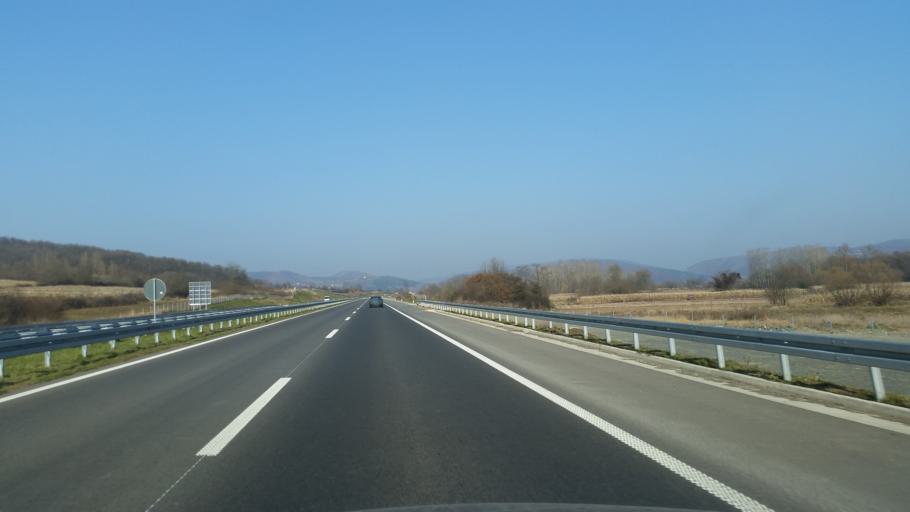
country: RS
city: Prislonica
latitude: 43.9377
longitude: 20.4009
